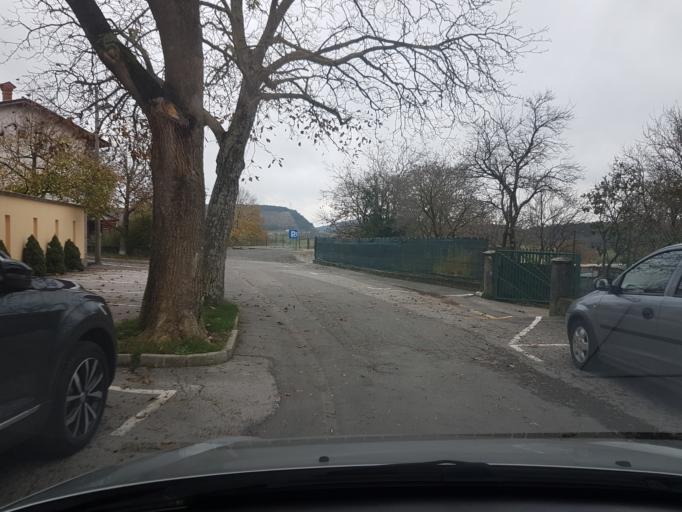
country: SI
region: Divaca
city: Divaca
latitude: 45.7315
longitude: 14.0116
